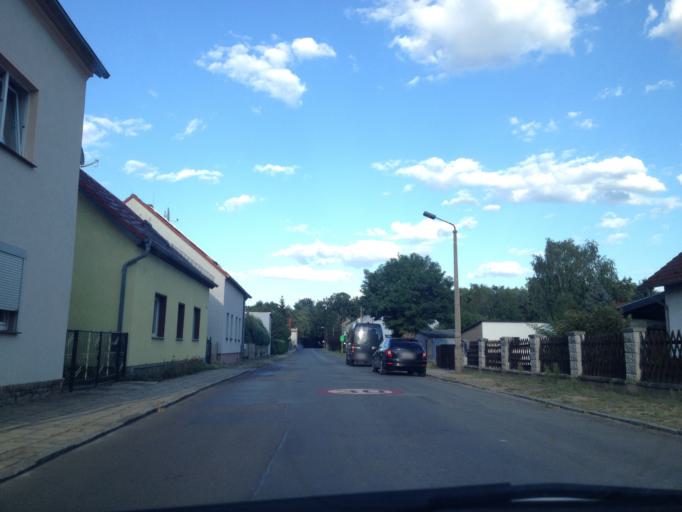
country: DE
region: Brandenburg
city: Vetschau
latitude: 51.7893
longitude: 14.0730
